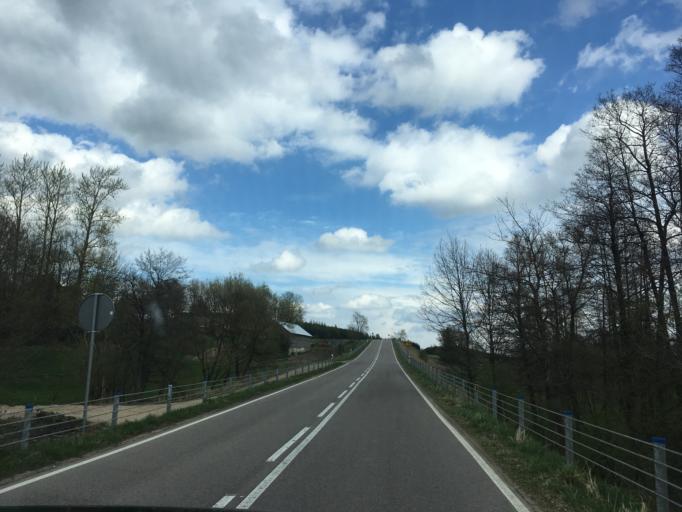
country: PL
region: Podlasie
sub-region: Powiat suwalski
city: Filipow
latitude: 54.3598
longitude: 22.8068
